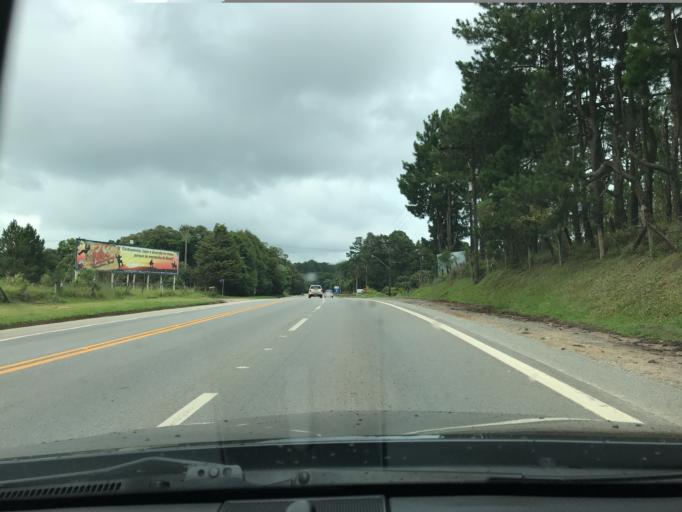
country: BR
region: Sao Paulo
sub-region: Vargem Grande Paulista
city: Vargem Grande Paulista
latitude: -23.5978
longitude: -47.0458
